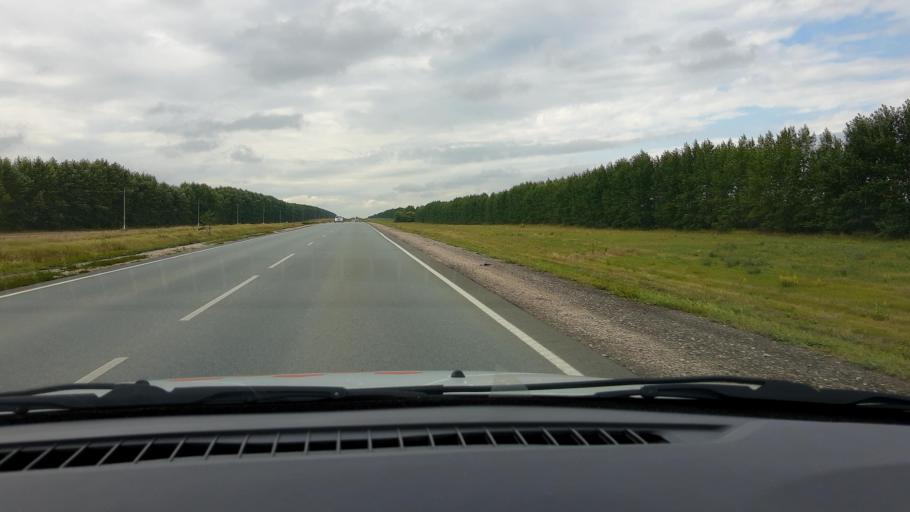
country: RU
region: Tatarstan
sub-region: Chistopol'skiy Rayon
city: Chistopol'
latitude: 55.3113
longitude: 50.3821
